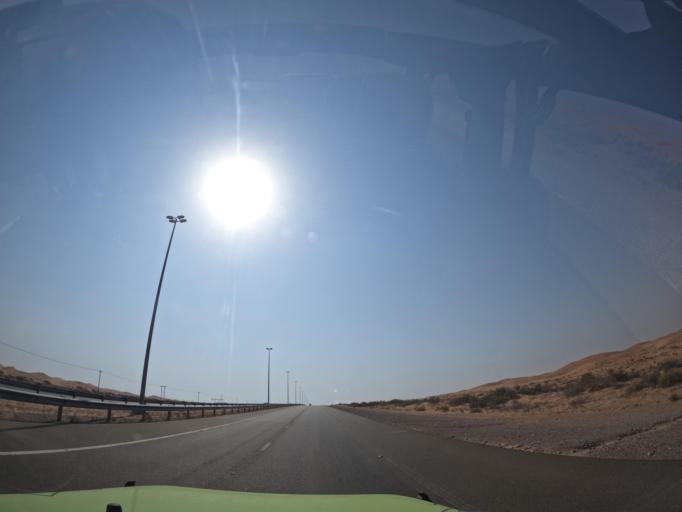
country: OM
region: Al Buraimi
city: Al Buraymi
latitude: 24.4486
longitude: 55.6551
